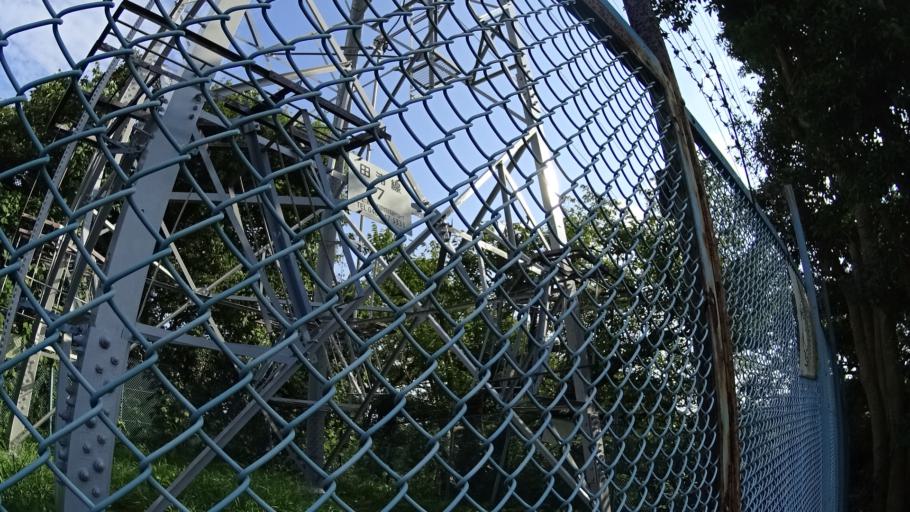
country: JP
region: Kanagawa
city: Yokosuka
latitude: 35.2870
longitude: 139.6324
